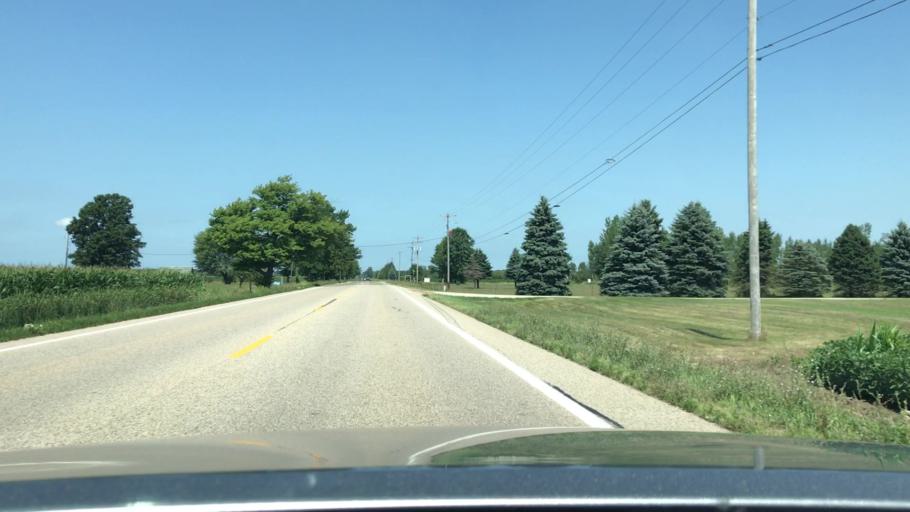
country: US
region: Michigan
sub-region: Ottawa County
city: Allendale
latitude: 42.9555
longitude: -86.0824
